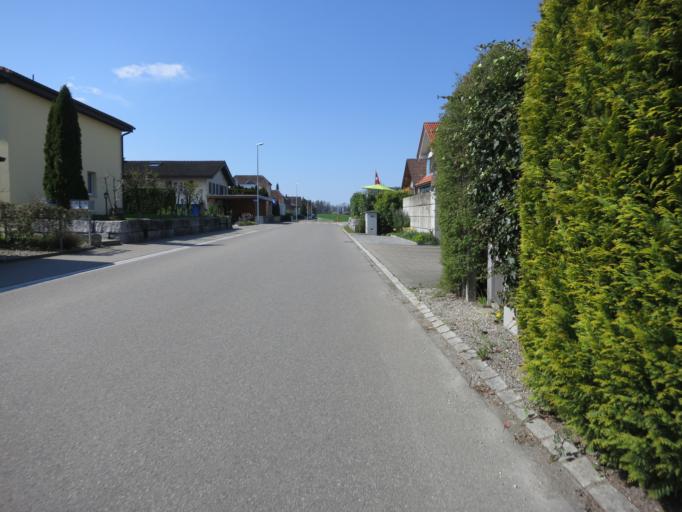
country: CH
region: Schwyz
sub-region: Bezirk March
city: Lachen
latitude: 47.1800
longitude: 8.8692
